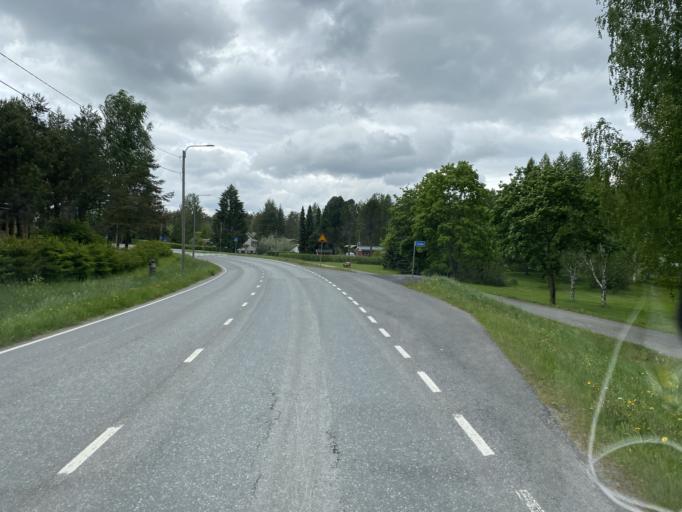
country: FI
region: Pirkanmaa
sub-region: Etelae-Pirkanmaa
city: Urjala
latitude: 61.0789
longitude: 23.5647
